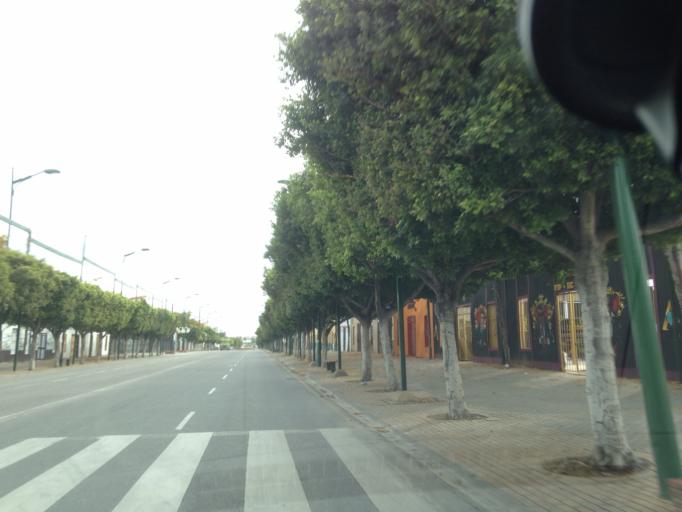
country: ES
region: Andalusia
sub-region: Provincia de Malaga
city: Malaga
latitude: 36.7060
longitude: -4.4648
